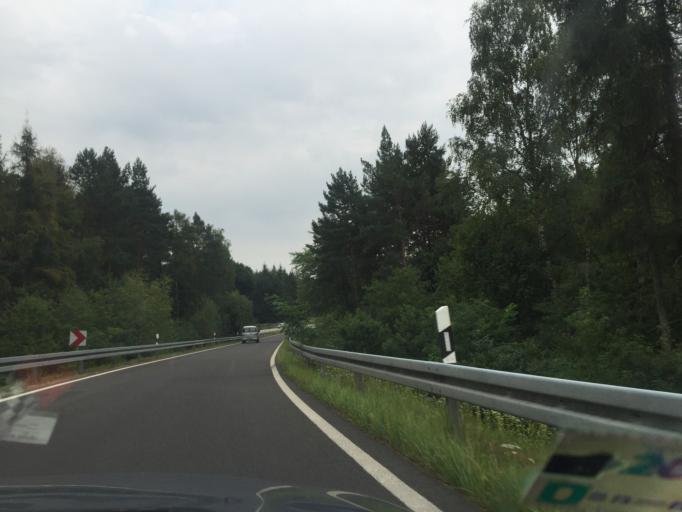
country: DE
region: Brandenburg
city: Bernau bei Berlin
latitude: 52.7283
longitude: 13.5389
